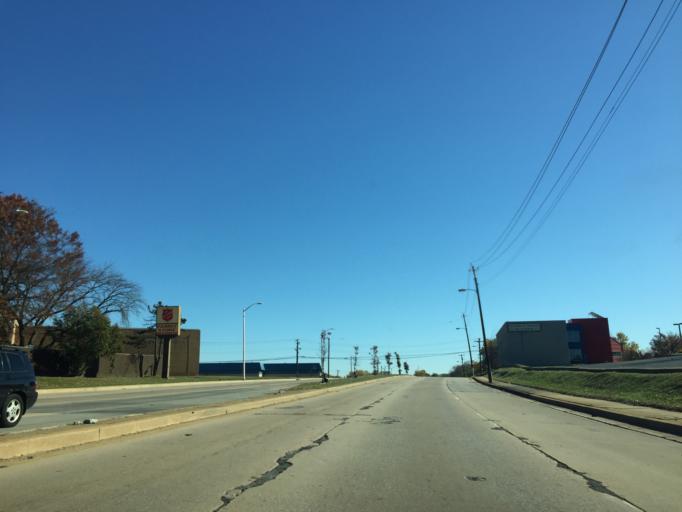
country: US
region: Maryland
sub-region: Baltimore County
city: Lansdowne
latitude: 39.2549
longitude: -76.6573
